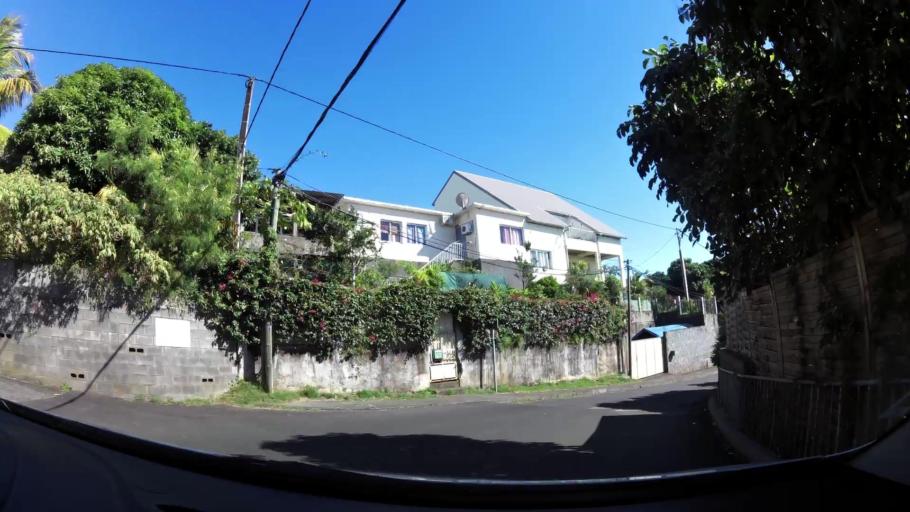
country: RE
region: Reunion
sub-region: Reunion
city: Saint-Denis
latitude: -20.9153
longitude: 55.4839
